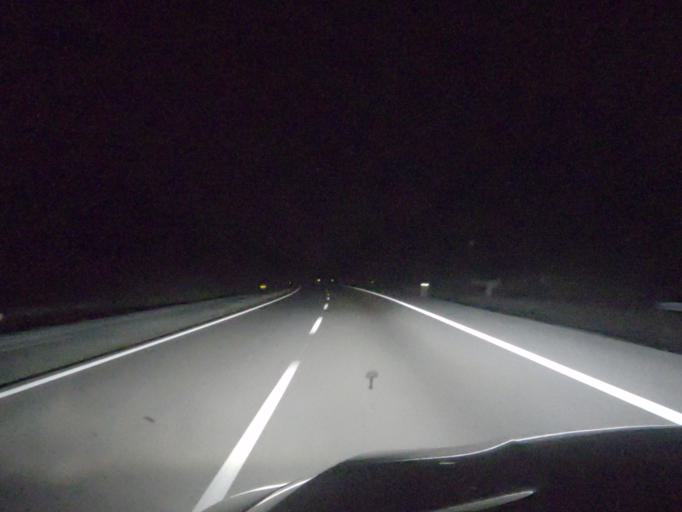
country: PT
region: Aveiro
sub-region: Oliveira do Bairro
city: Oia
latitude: 40.5125
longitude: -8.5387
